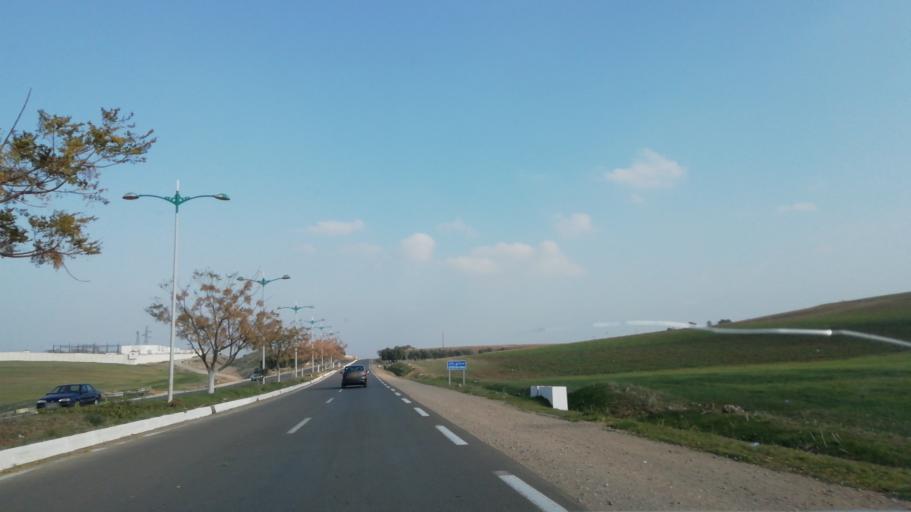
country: DZ
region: Ain Temouchent
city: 'Ain Temouchent
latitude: 35.2930
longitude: -1.1148
